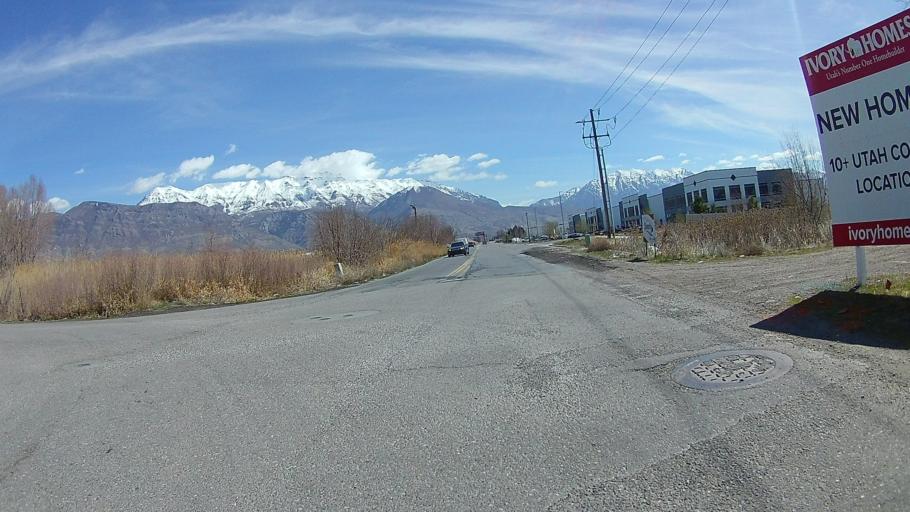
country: US
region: Utah
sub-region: Utah County
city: American Fork
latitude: 40.3550
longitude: -111.7858
